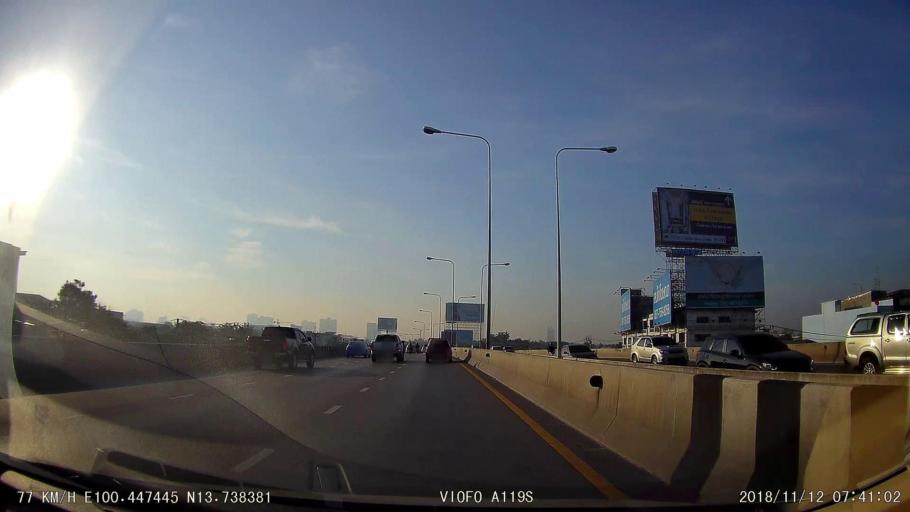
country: TH
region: Bangkok
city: Phasi Charoen
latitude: 13.7385
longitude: 100.4474
